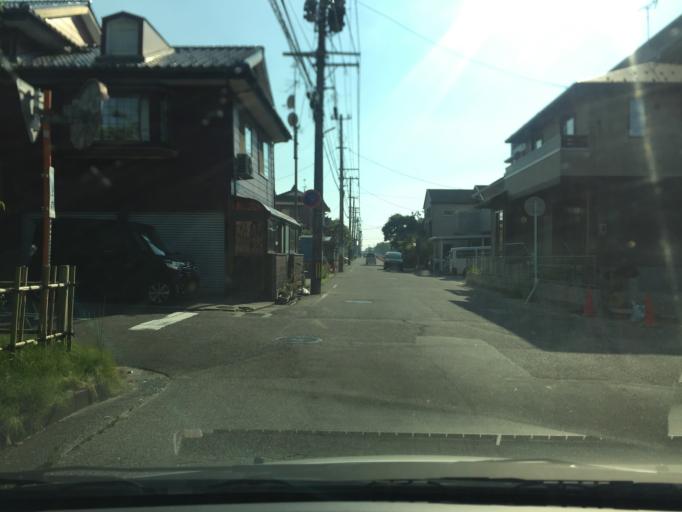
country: JP
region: Niigata
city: Niigata-shi
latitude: 37.8925
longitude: 139.0500
